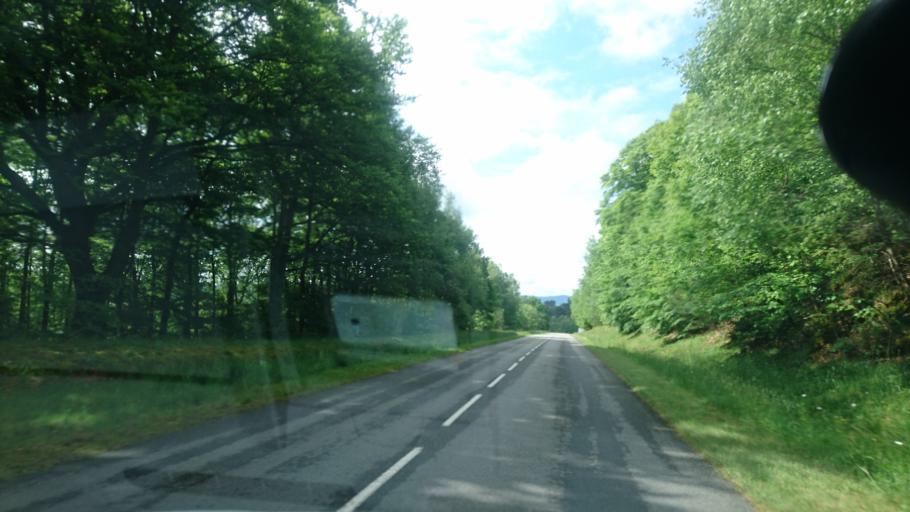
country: FR
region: Limousin
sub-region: Departement de la Haute-Vienne
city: Peyrat-le-Chateau
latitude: 45.7862
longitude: 1.8491
